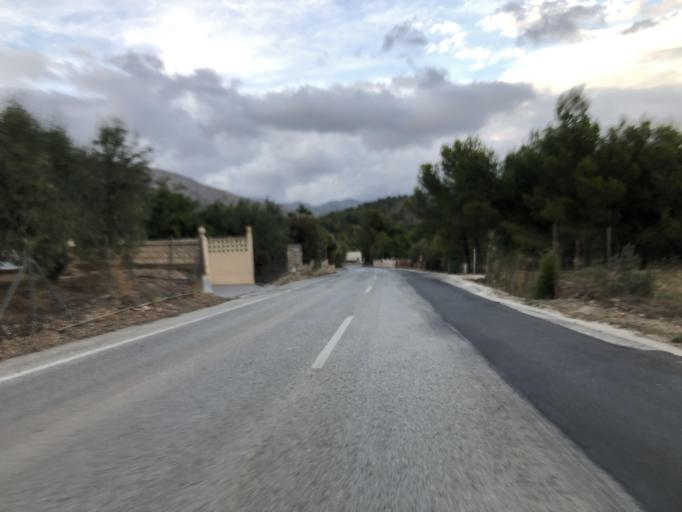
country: ES
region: Valencia
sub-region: Provincia de Alicante
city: Polop
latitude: 38.6311
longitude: -0.1465
